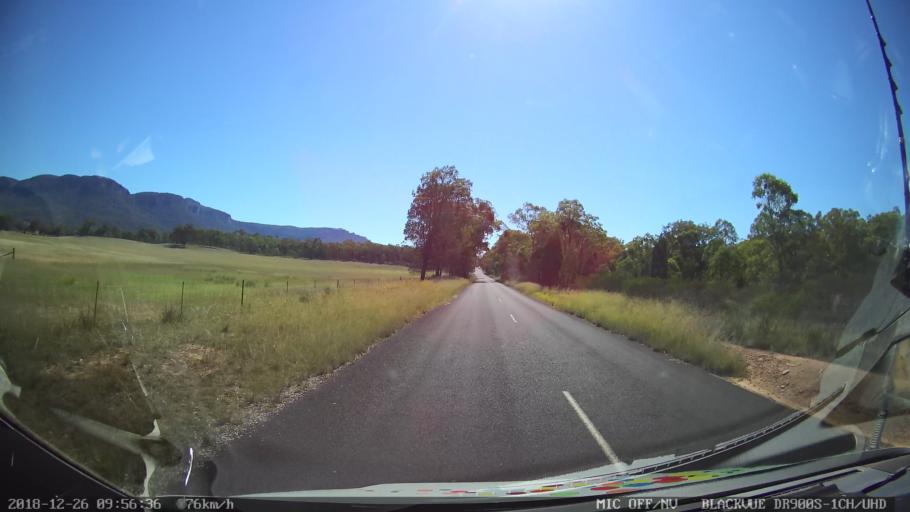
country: AU
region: New South Wales
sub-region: Mid-Western Regional
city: Kandos
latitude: -33.0403
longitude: 150.1814
